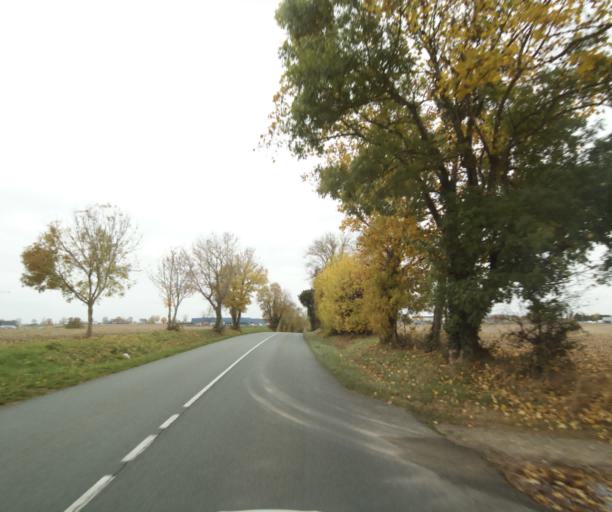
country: FR
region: Poitou-Charentes
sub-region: Departement de la Charente-Maritime
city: Les Gonds
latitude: 45.7147
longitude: -0.6448
